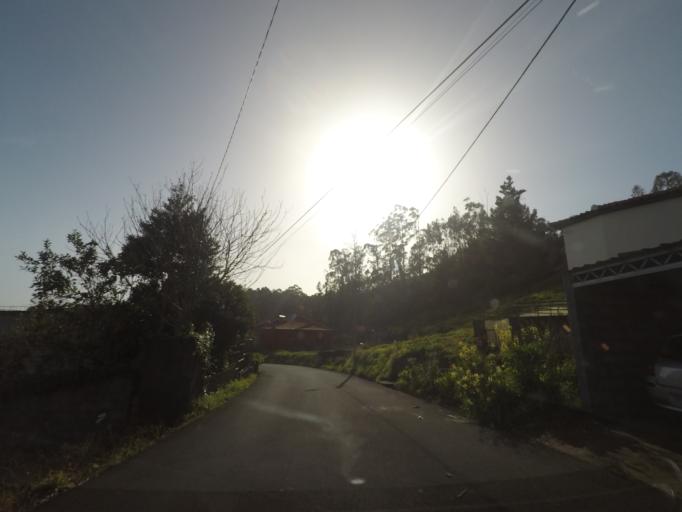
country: PT
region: Madeira
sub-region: Ribeira Brava
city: Campanario
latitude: 32.6813
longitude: -17.0074
